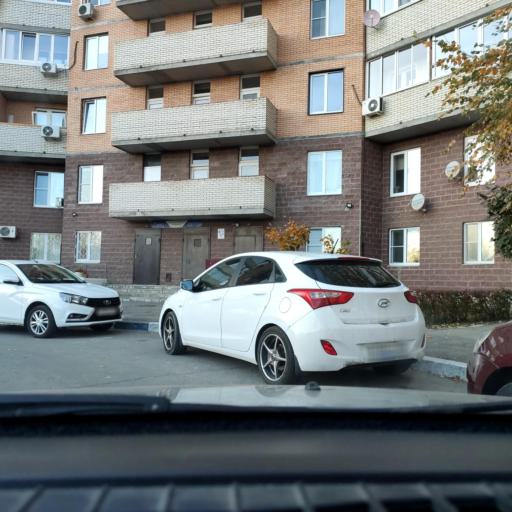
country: RU
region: Samara
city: Tol'yatti
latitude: 53.4994
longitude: 49.2853
